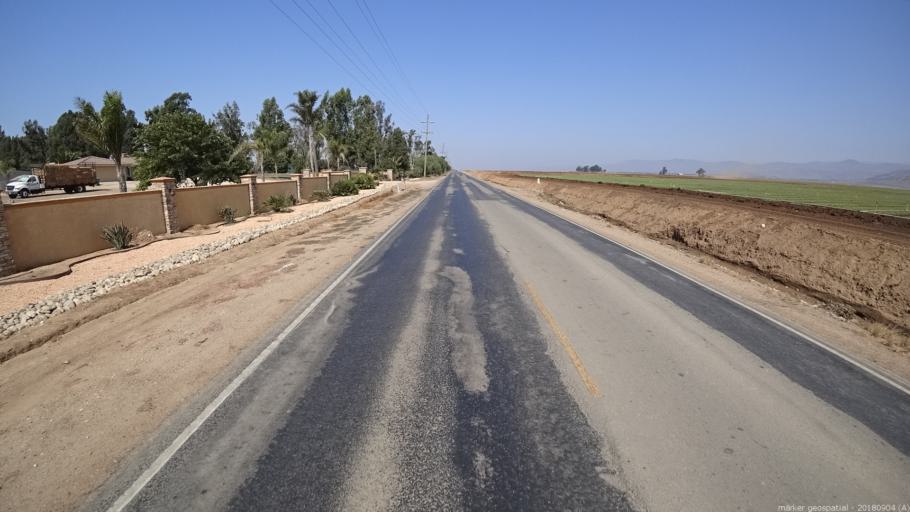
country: US
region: California
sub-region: Monterey County
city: Gonzales
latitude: 36.5463
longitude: -121.4700
